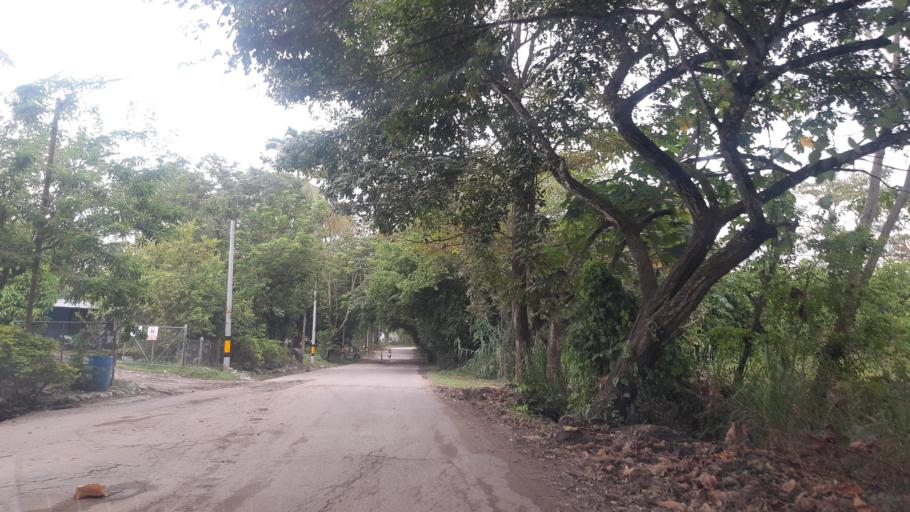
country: CO
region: Antioquia
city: Puerto Triunfo
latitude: 5.8789
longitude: -74.6350
